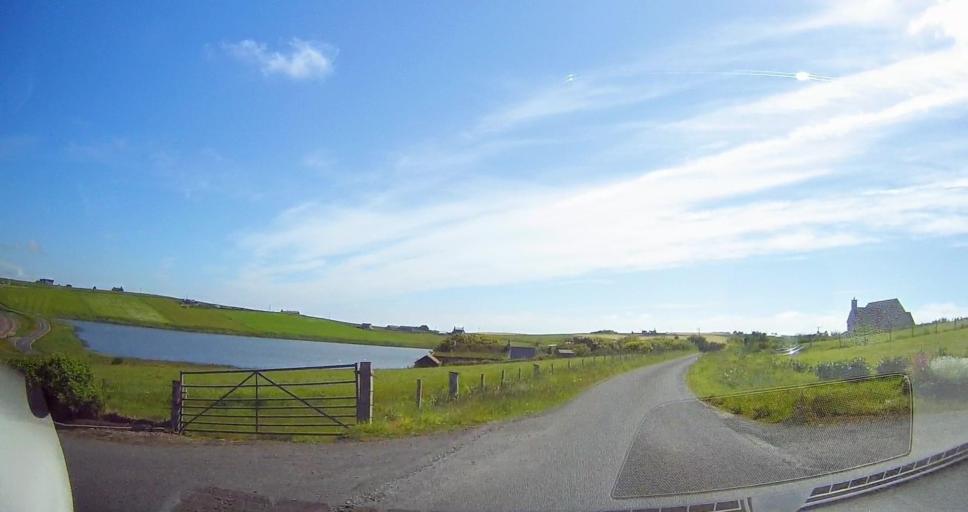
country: GB
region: Scotland
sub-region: Orkney Islands
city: Kirkwall
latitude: 58.8537
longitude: -2.9195
